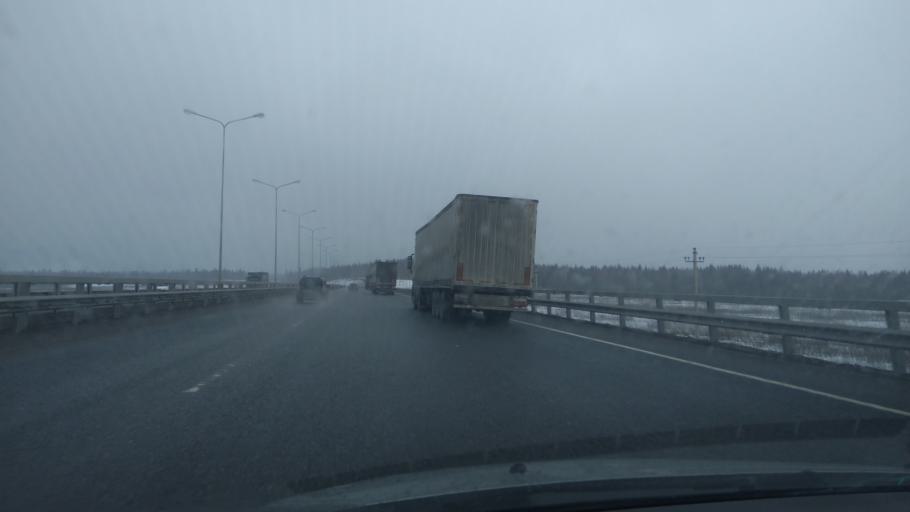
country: RU
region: Perm
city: Zvezdnyy
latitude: 57.7720
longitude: 56.3368
